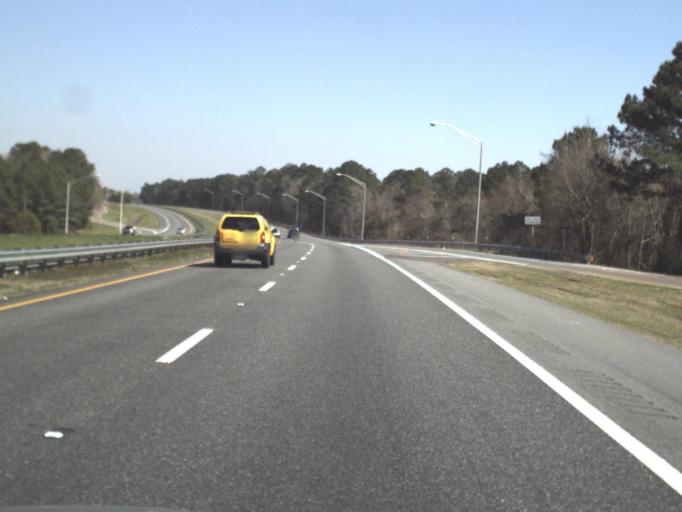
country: US
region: Florida
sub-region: Jackson County
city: Marianna
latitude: 30.7566
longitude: -85.3275
